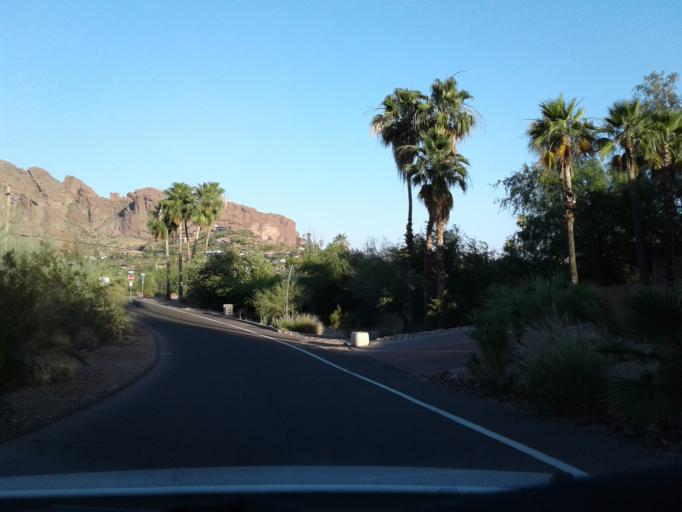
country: US
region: Arizona
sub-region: Maricopa County
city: Paradise Valley
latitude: 33.5241
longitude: -111.9874
